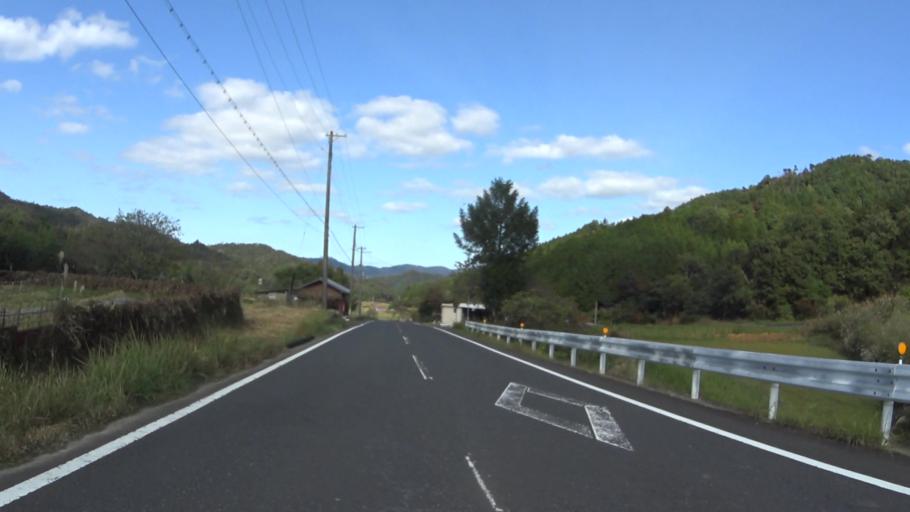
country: JP
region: Hyogo
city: Toyooka
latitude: 35.5460
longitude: 134.9782
